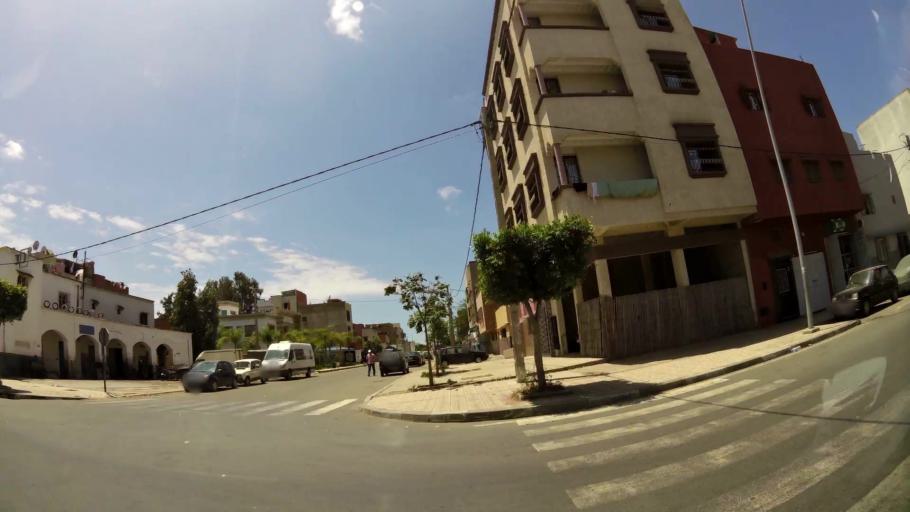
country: MA
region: Gharb-Chrarda-Beni Hssen
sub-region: Kenitra Province
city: Kenitra
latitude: 34.2579
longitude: -6.5604
